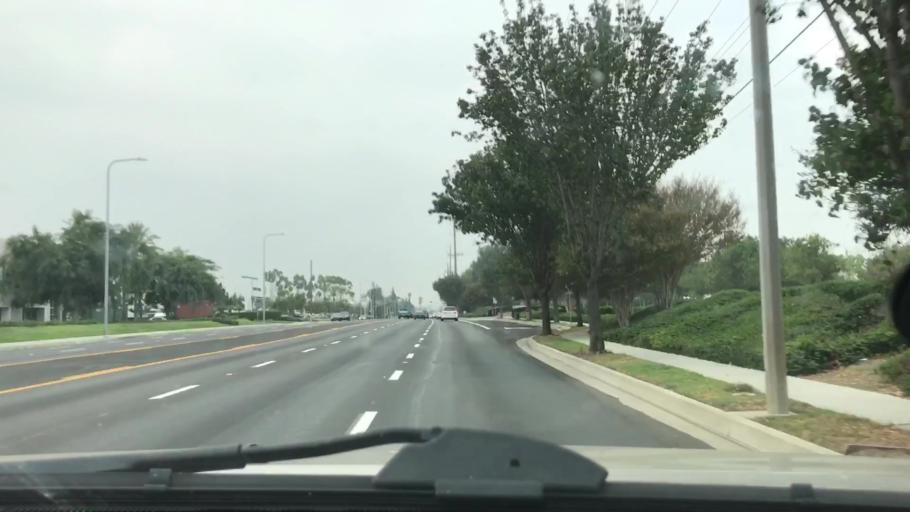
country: US
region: California
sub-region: Los Angeles County
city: Carson
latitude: 33.8526
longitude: -118.3095
